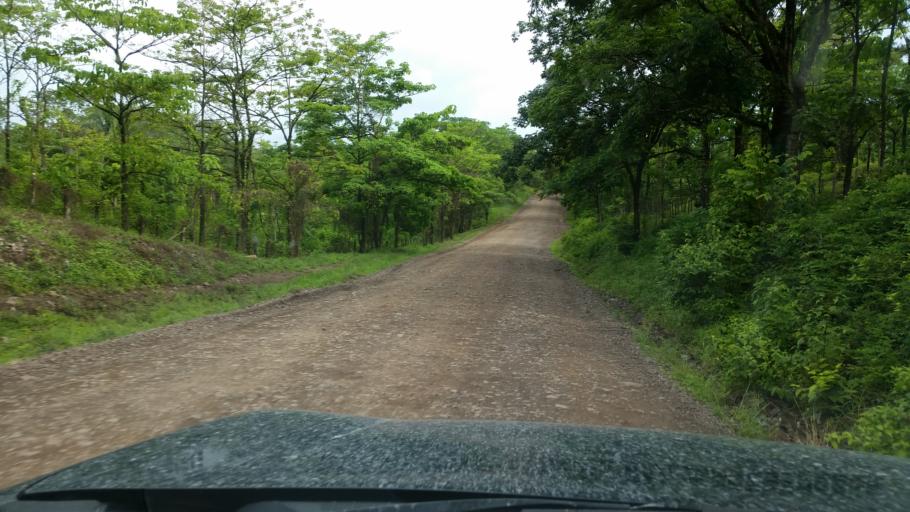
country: NI
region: Atlantico Norte (RAAN)
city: Siuna
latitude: 13.4611
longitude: -84.8494
